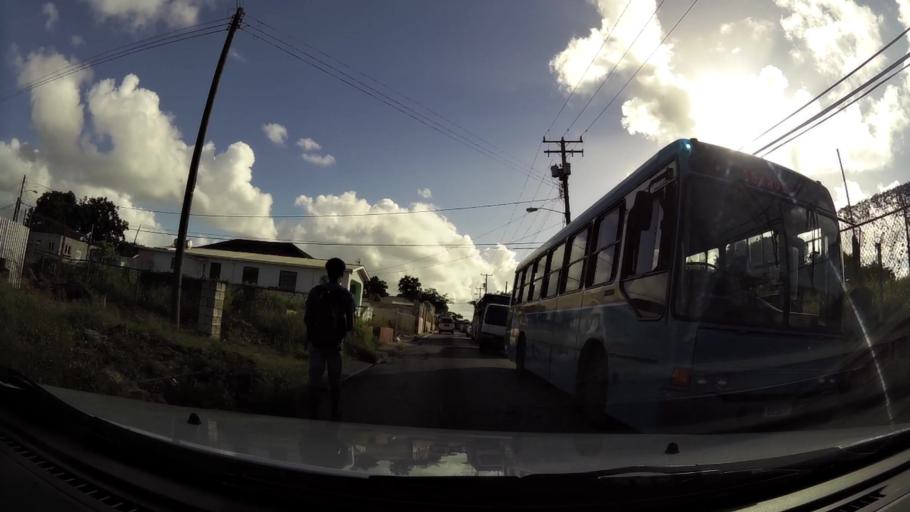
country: BB
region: Saint Michael
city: Bridgetown
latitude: 13.1022
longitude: -59.5967
